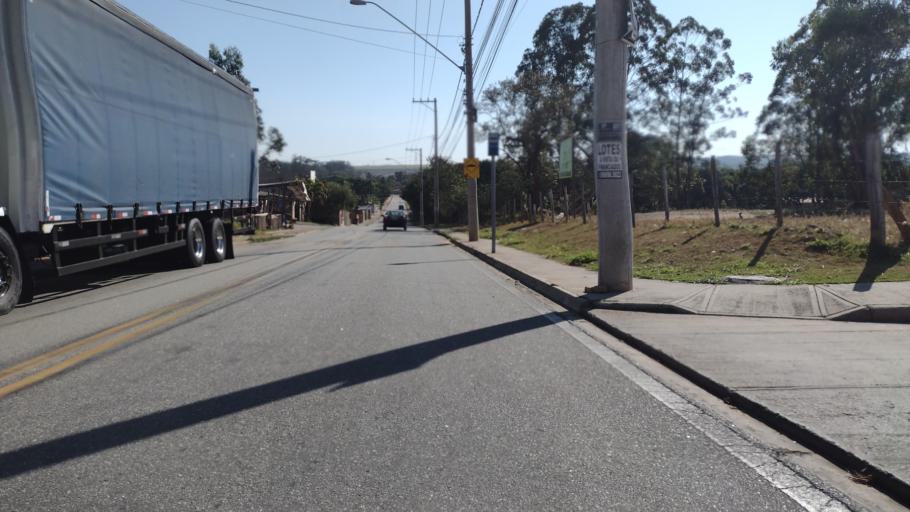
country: BR
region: Sao Paulo
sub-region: Sorocaba
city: Sorocaba
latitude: -23.4156
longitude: -47.4796
